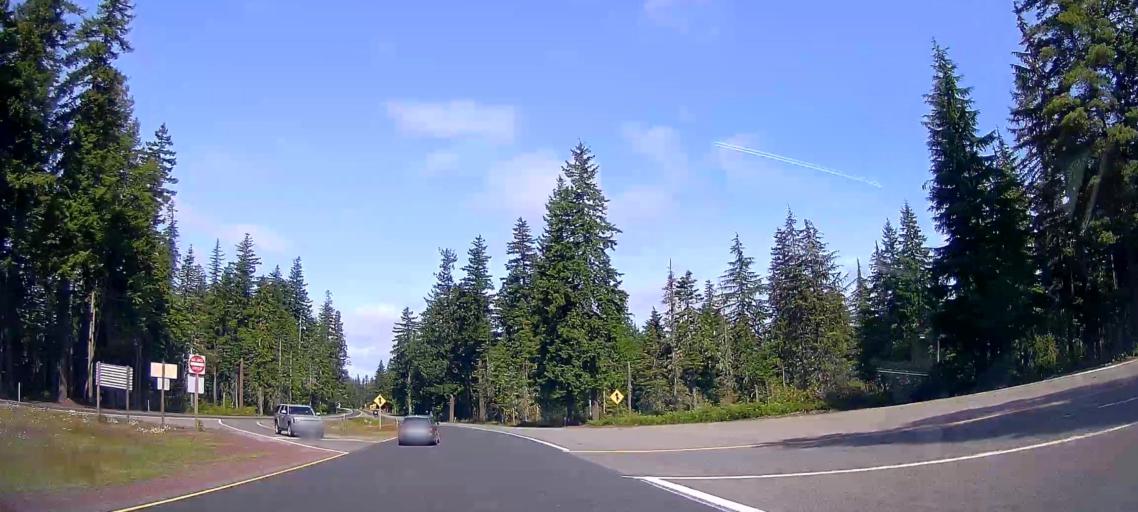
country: US
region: Oregon
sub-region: Clackamas County
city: Mount Hood Village
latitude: 45.1311
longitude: -121.6014
